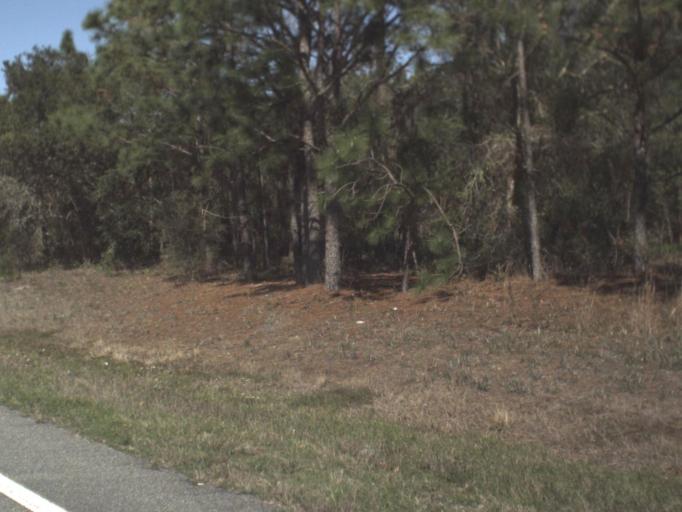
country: US
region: Florida
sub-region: Wakulla County
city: Crawfordville
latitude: 29.9556
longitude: -84.3852
